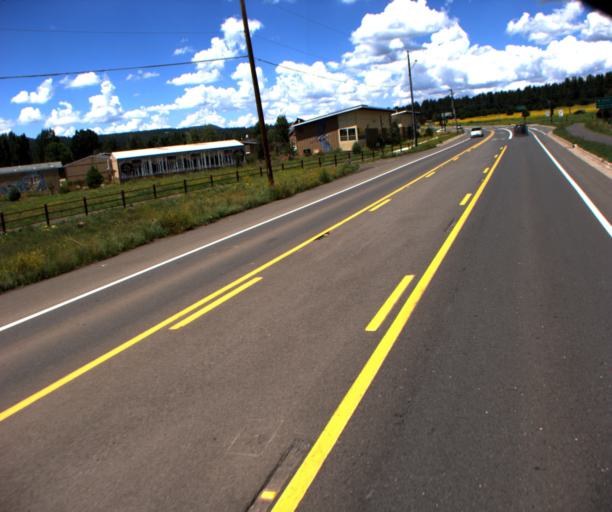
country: US
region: Arizona
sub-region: Coconino County
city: Flagstaff
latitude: 35.2375
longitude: -111.6677
